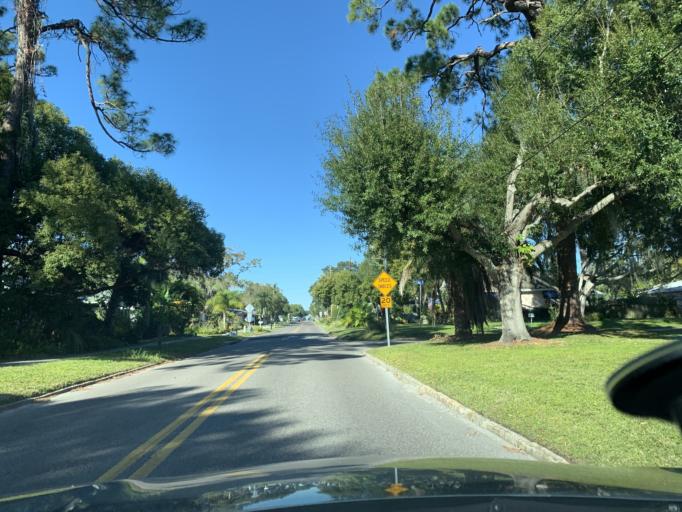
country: US
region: Florida
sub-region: Pinellas County
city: Gulfport
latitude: 27.7401
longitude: -82.6997
